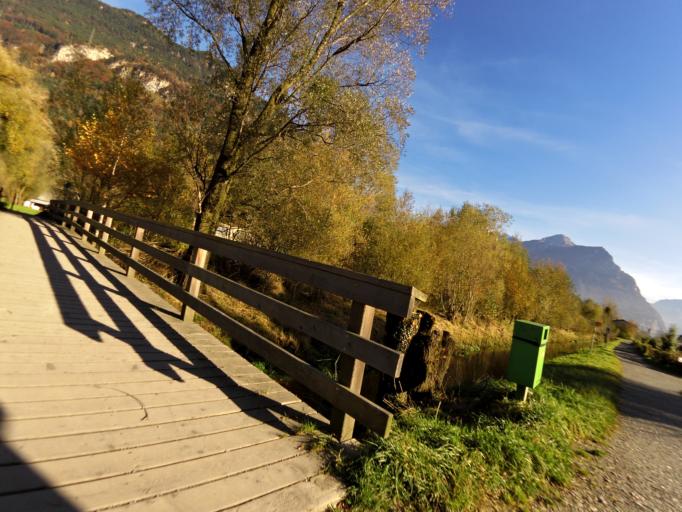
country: CH
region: Uri
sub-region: Uri
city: Flueelen
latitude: 46.8975
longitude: 8.6191
